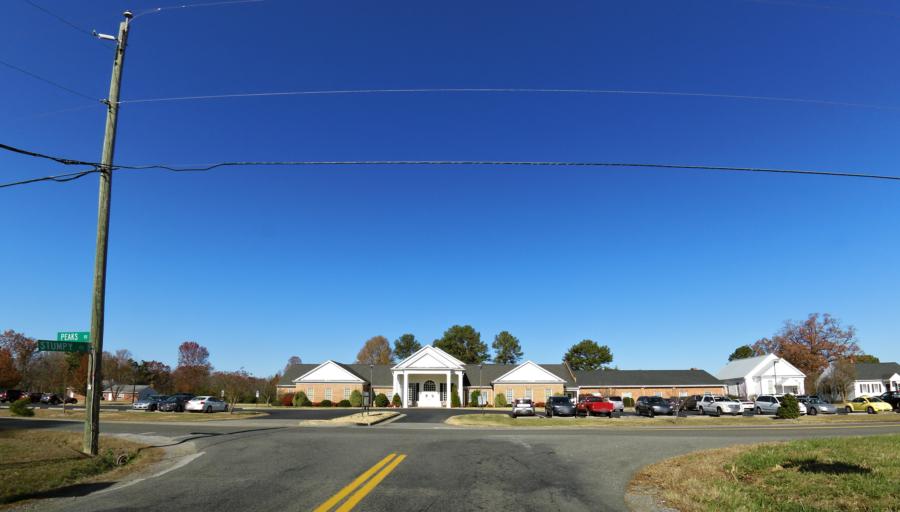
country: US
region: Virginia
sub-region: Hanover County
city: Hanover
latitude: 37.7190
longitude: -77.4014
